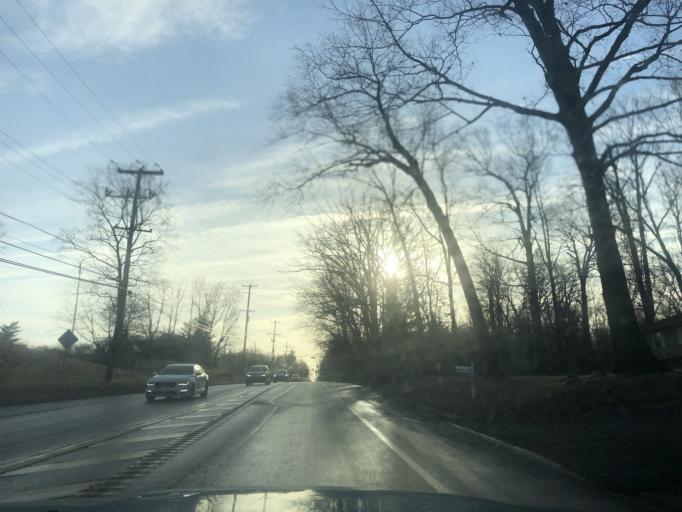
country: US
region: Pennsylvania
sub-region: Montgomery County
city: Dresher
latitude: 40.1379
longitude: -75.1619
